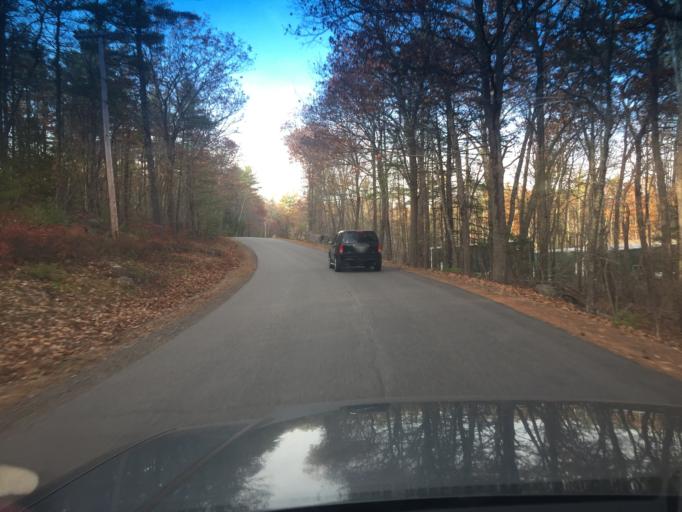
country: US
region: Maine
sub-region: York County
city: Eliot
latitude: 43.1915
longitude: -70.7480
